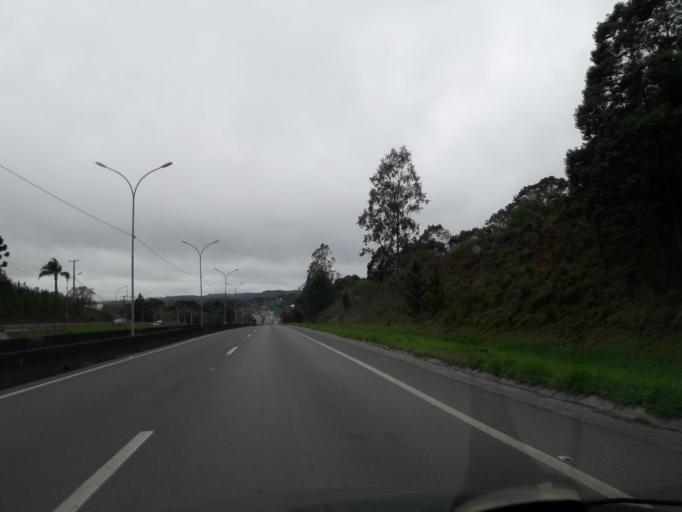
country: BR
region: Parana
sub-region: Quatro Barras
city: Quatro Barras
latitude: -25.3503
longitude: -49.0571
